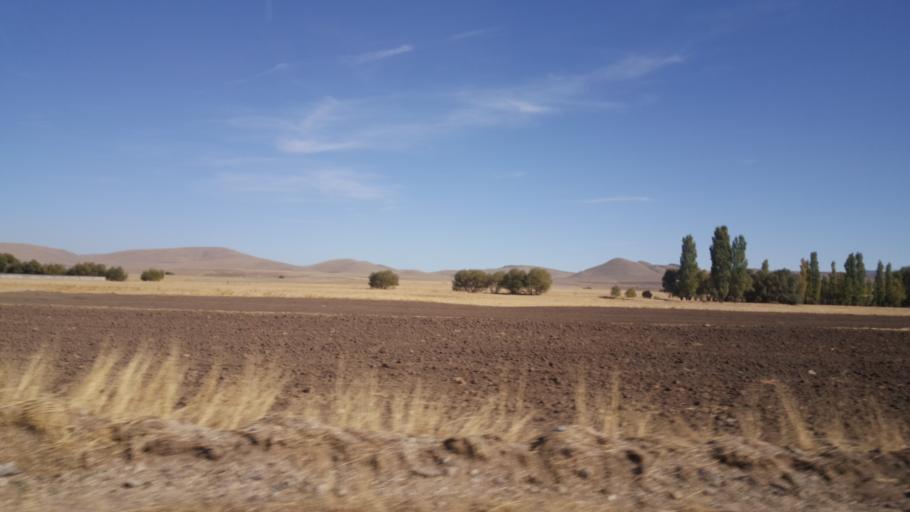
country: TR
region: Ankara
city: Altpinar
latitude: 39.2737
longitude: 32.7548
